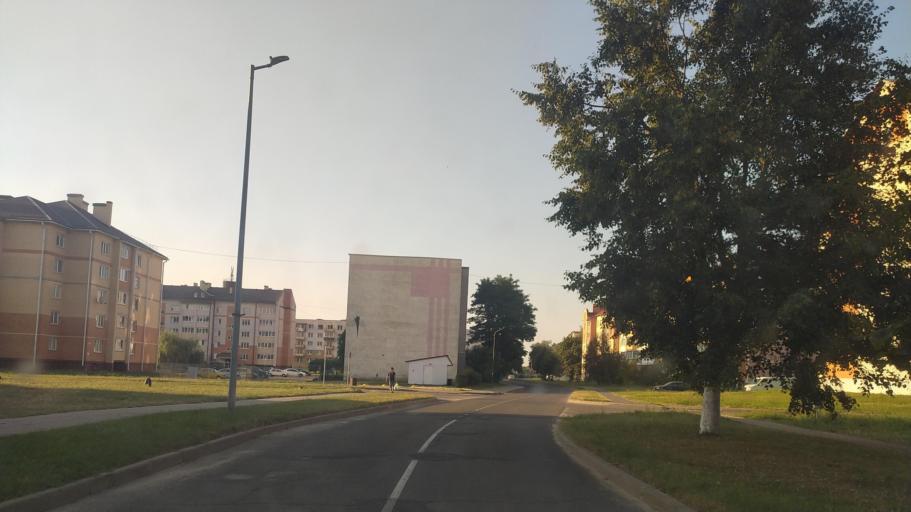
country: BY
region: Brest
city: Byaroza
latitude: 52.5445
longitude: 24.9845
